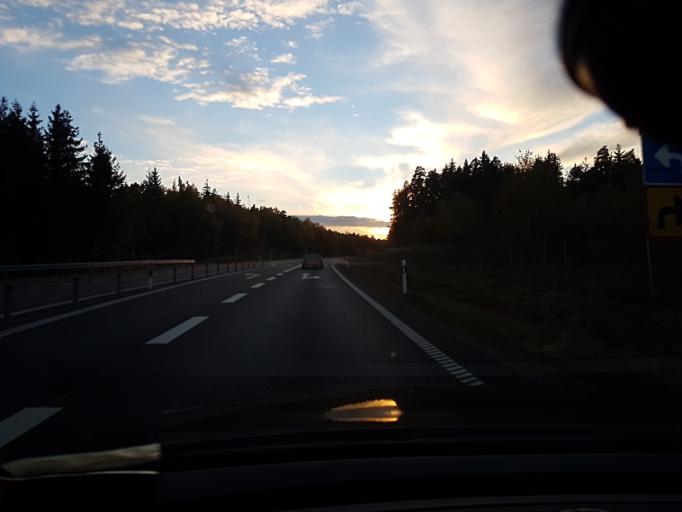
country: SE
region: Kronoberg
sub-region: Ljungby Kommun
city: Ljungby
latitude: 56.7630
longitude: 13.7887
